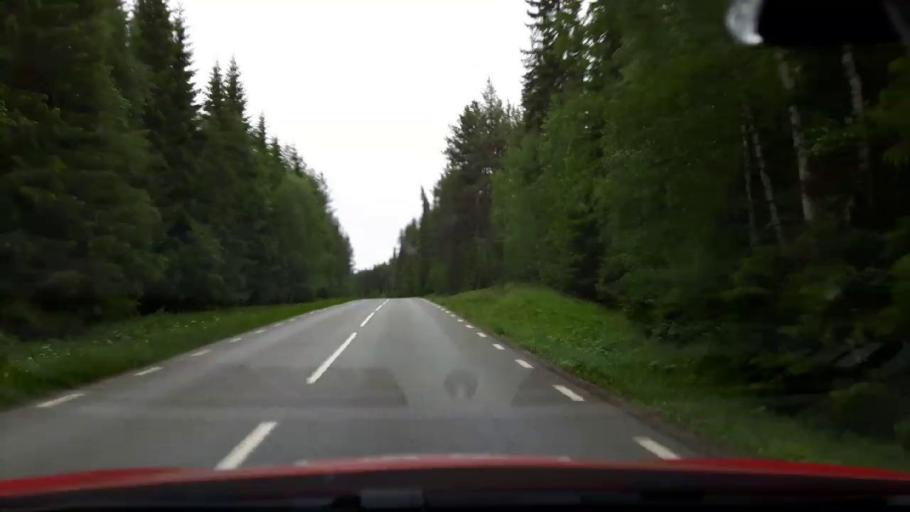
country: SE
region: Jaemtland
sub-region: Stroemsunds Kommun
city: Stroemsund
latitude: 63.4615
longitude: 15.4571
